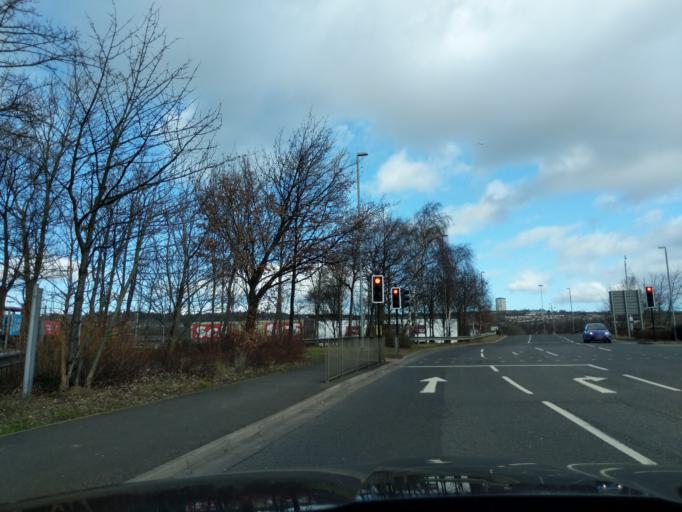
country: GB
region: England
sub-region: Gateshead
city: Whickham
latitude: 54.9595
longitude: -1.6741
